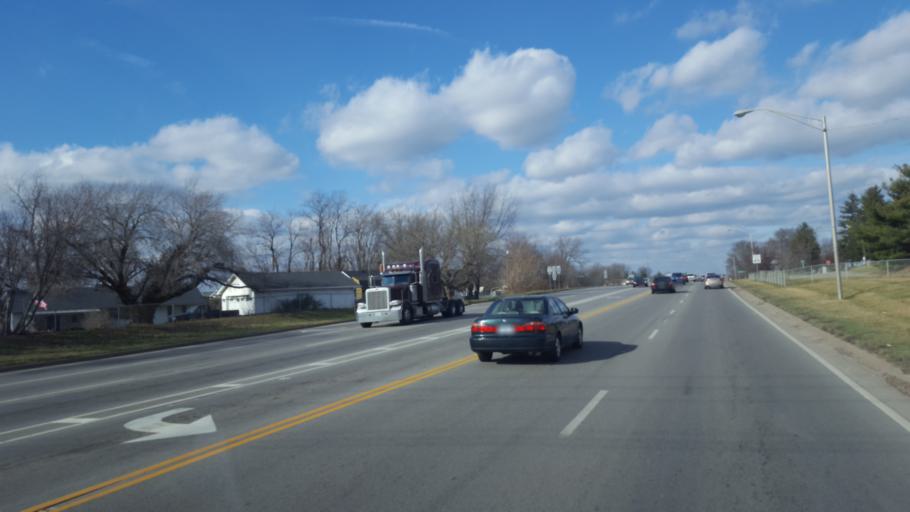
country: US
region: Kentucky
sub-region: Scott County
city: Georgetown
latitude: 38.2148
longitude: -84.5404
